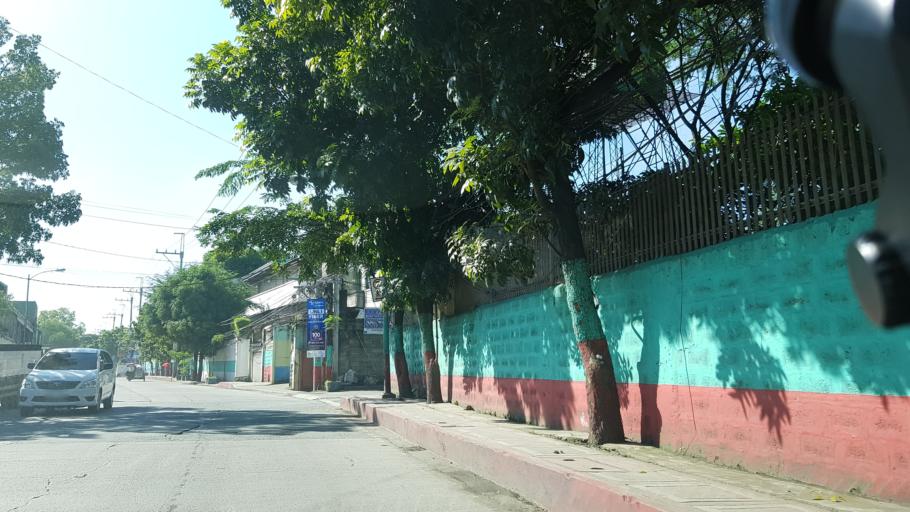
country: PH
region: Calabarzon
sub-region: Province of Rizal
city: Pateros
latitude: 14.5604
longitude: 121.0948
